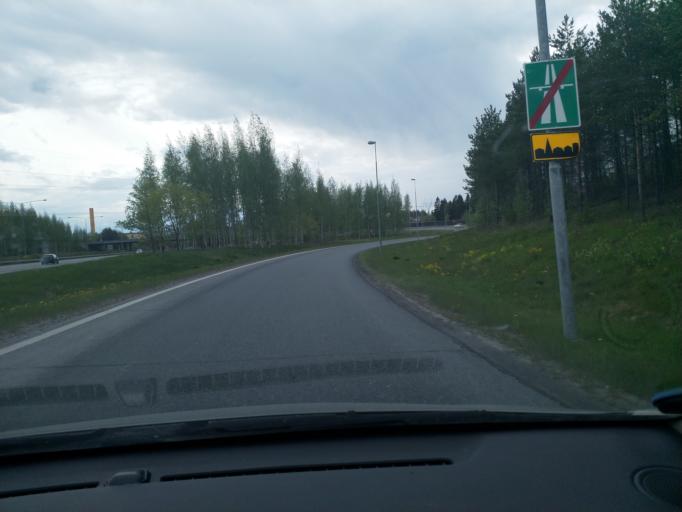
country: FI
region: Pirkanmaa
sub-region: Tampere
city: Tampere
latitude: 61.4613
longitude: 23.7970
